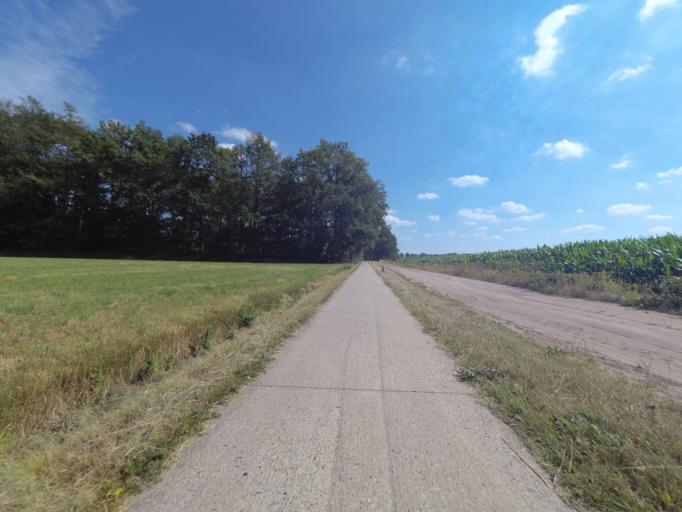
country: NL
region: Overijssel
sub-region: Gemeente Oldenzaal
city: Oldenzaal
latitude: 52.3719
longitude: 6.8994
